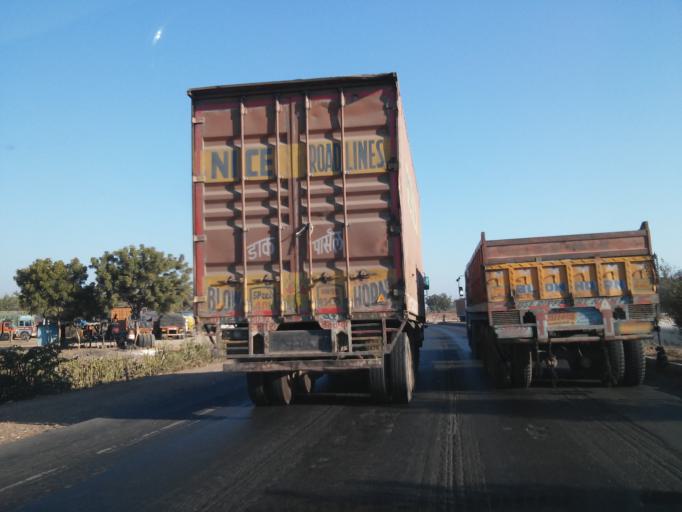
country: IN
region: Rajasthan
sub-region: Dungarpur
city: Dungarpur
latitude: 24.0104
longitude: 73.6571
